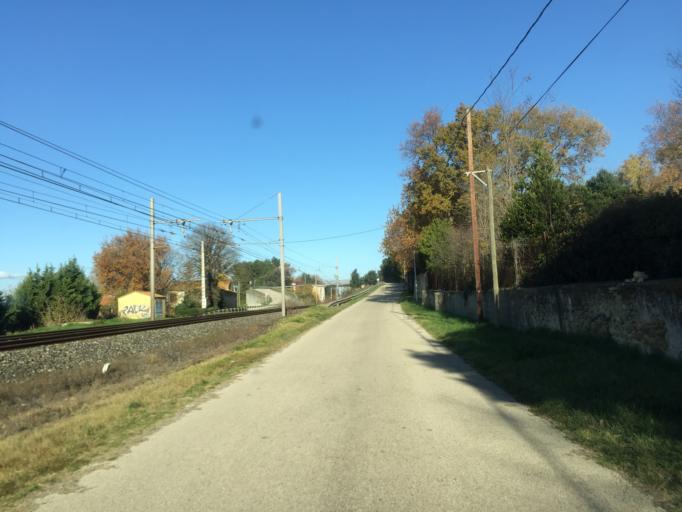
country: FR
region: Provence-Alpes-Cote d'Azur
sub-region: Departement du Vaucluse
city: Courthezon
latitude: 44.0674
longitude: 4.8919
